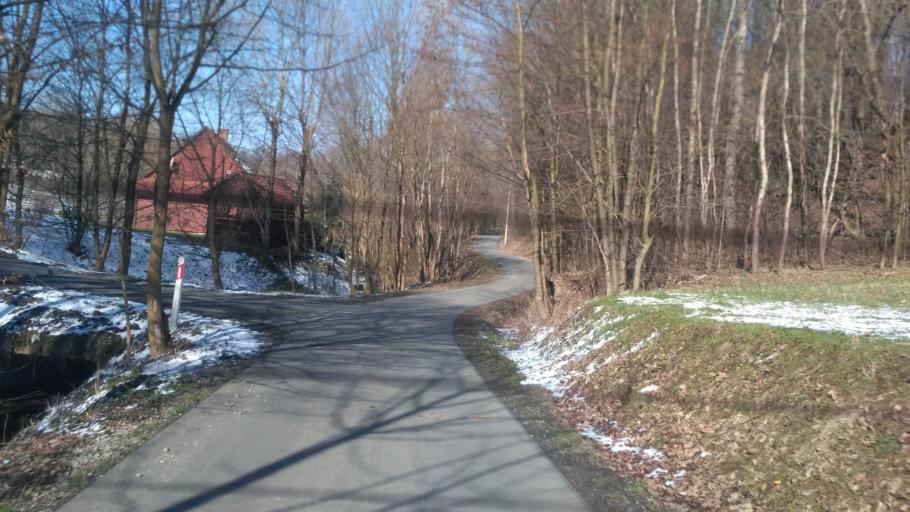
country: PL
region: Subcarpathian Voivodeship
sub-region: Powiat strzyzowski
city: Gwoznica Gorna
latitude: 49.8260
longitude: 22.0027
